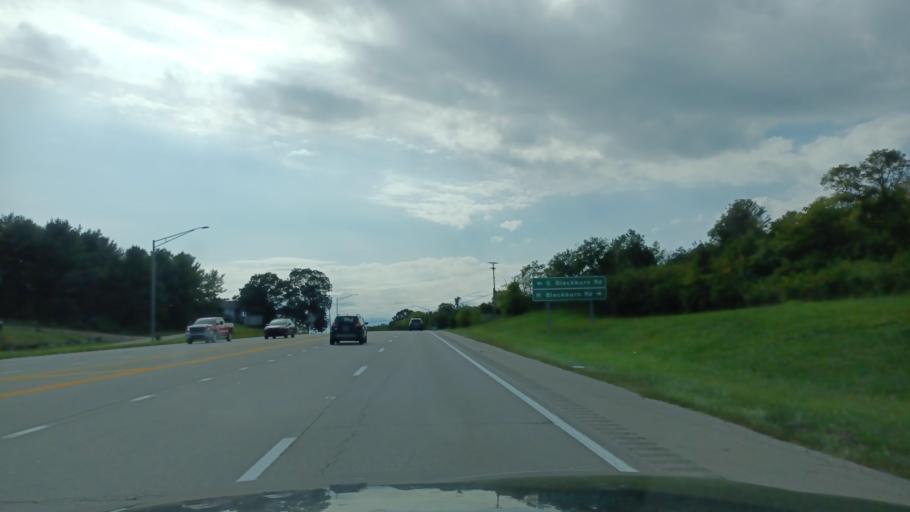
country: US
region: Ohio
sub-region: Athens County
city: Athens
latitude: 39.3003
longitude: -82.1102
